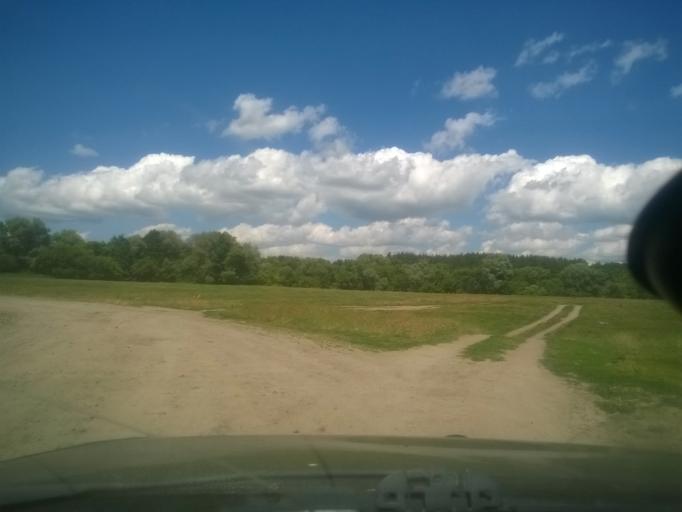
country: RU
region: Kursk
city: Kursk
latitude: 51.6840
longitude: 36.1148
